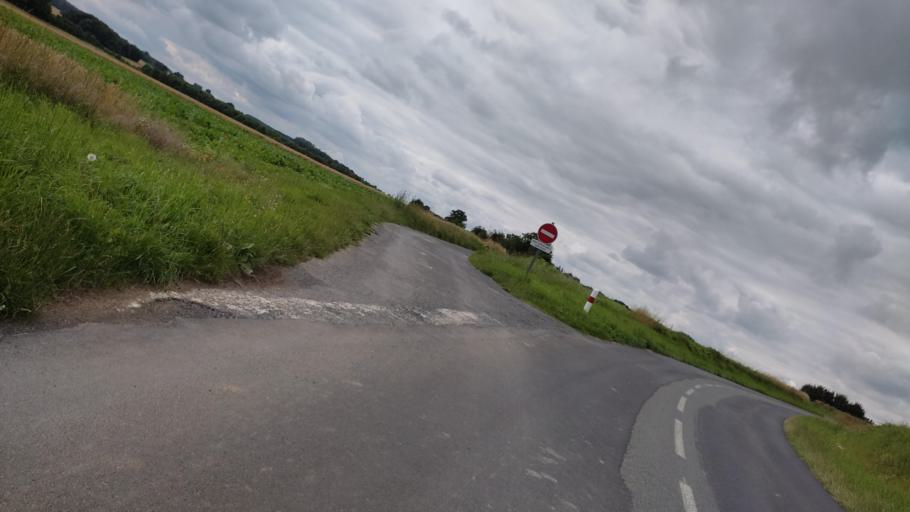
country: FR
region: Nord-Pas-de-Calais
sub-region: Departement du Pas-de-Calais
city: Beaumetz-les-Loges
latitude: 50.2633
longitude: 2.6635
